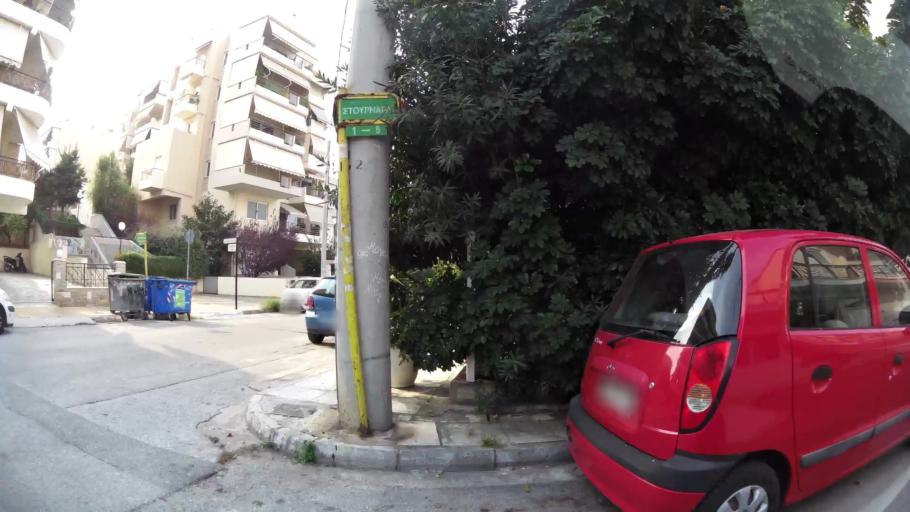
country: GR
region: Attica
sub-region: Nomarchia Athinas
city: Agios Dimitrios
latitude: 37.9269
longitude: 23.7188
